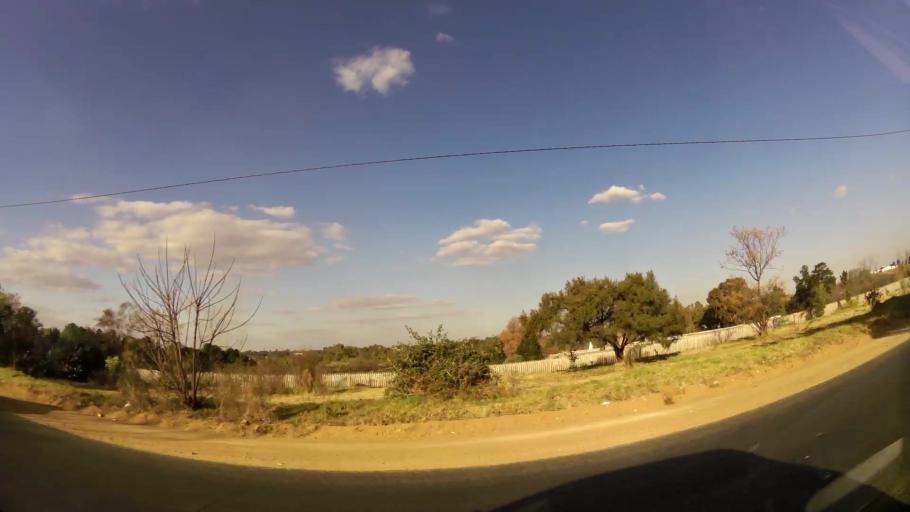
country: ZA
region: Gauteng
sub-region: City of Johannesburg Metropolitan Municipality
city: Midrand
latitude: -25.9750
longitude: 28.1351
